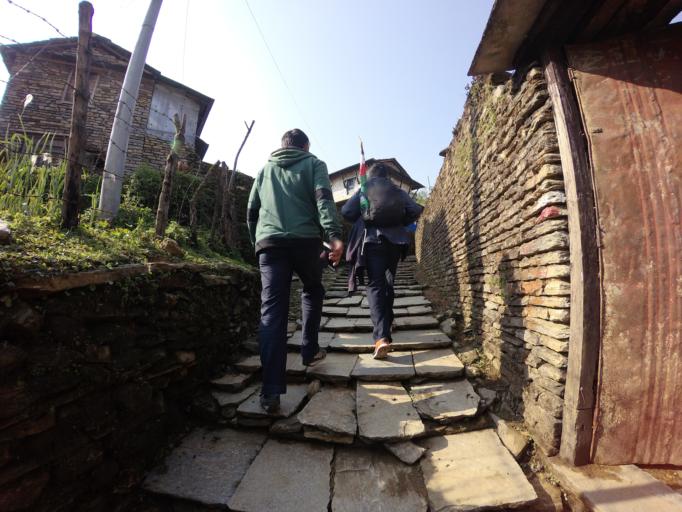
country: NP
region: Western Region
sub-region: Dhawalagiri Zone
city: Chitre
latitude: 28.3809
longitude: 83.8057
